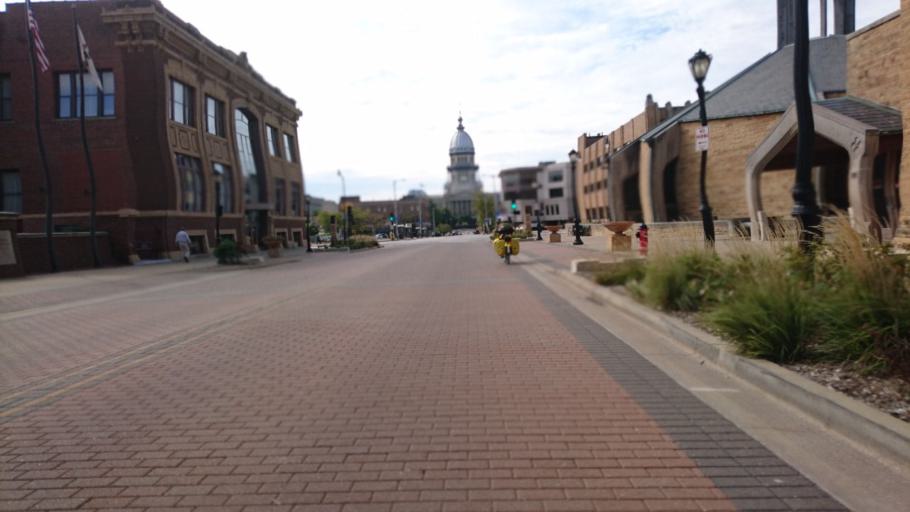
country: US
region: Illinois
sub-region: Sangamon County
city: Springfield
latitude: 39.7985
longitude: -89.6485
